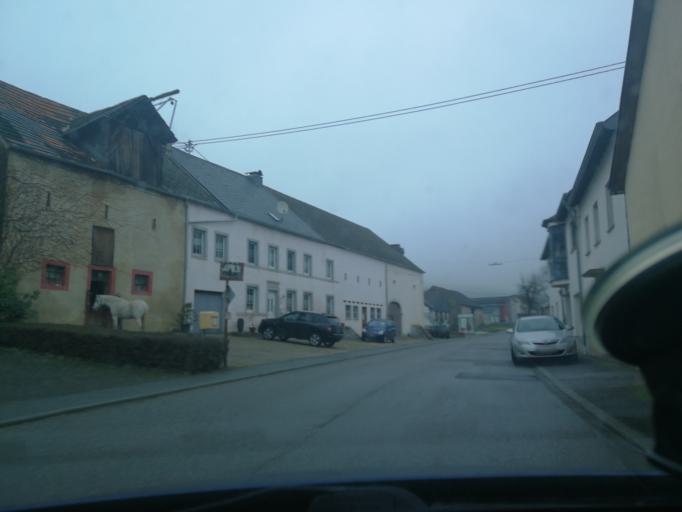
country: DE
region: Rheinland-Pfalz
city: Oberbillig
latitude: 49.7446
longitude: 6.5188
